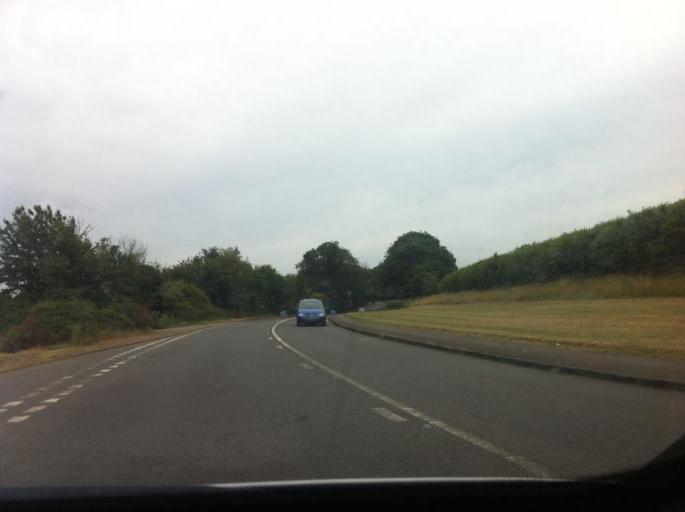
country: GB
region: England
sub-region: Northamptonshire
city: Earls Barton
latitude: 52.2662
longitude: -0.7910
